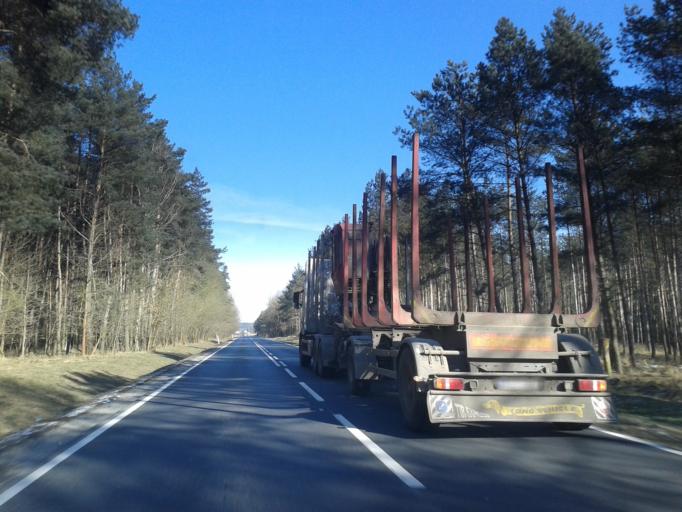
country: PL
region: Greater Poland Voivodeship
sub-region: Powiat pilski
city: Pila
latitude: 53.2067
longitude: 16.7808
